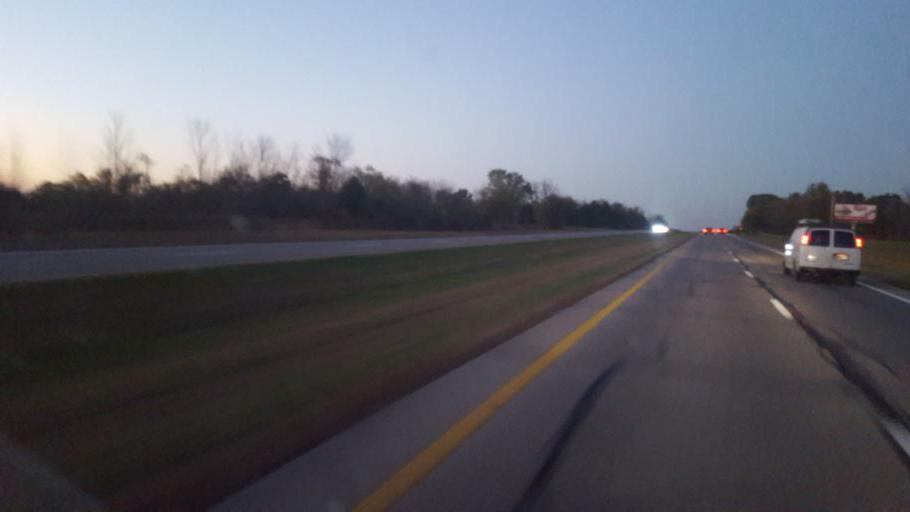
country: US
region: Ohio
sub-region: Pickaway County
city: Logan Elm Village
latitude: 39.5107
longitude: -82.9729
